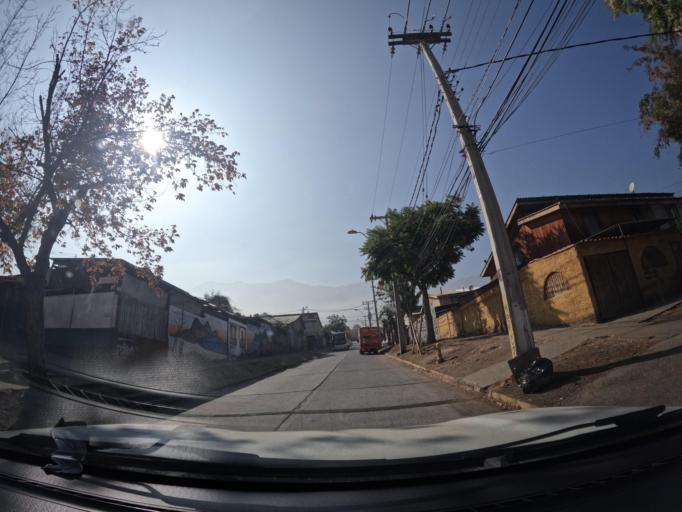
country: CL
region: Santiago Metropolitan
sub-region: Provincia de Santiago
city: Villa Presidente Frei, Nunoa, Santiago, Chile
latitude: -33.4748
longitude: -70.5367
